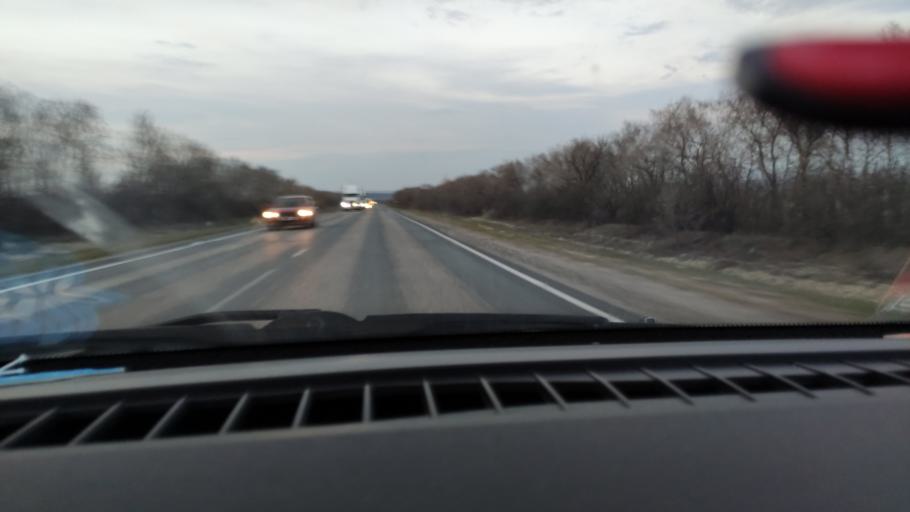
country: RU
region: Saratov
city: Sinodskoye
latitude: 51.9505
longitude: 46.6081
